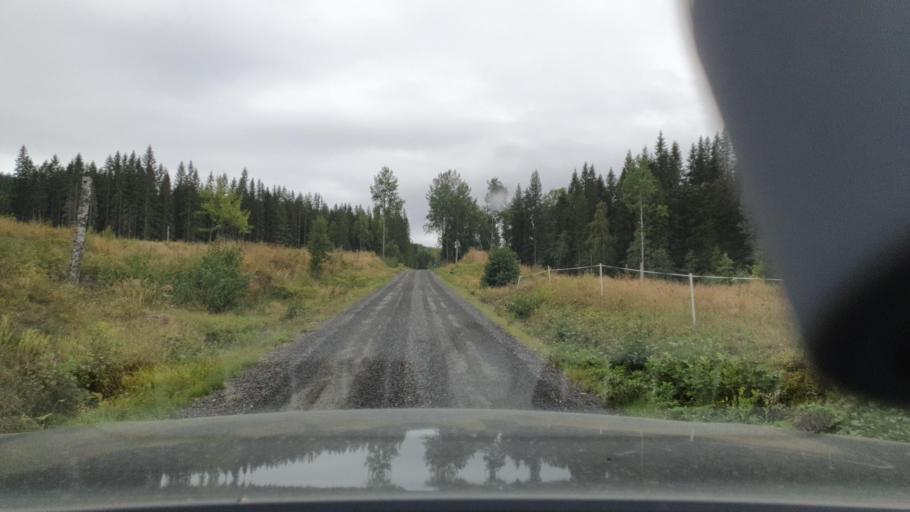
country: SE
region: Vaermland
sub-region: Torsby Kommun
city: Torsby
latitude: 60.3470
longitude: 12.6368
